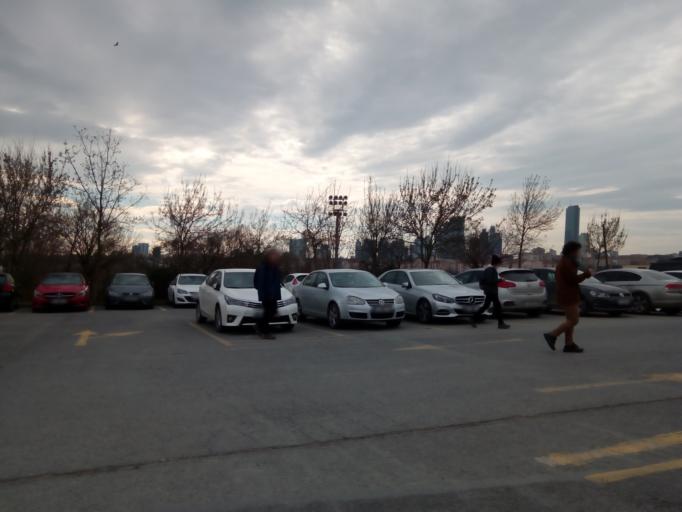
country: TR
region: Istanbul
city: Sisli
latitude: 41.1031
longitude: 29.0239
